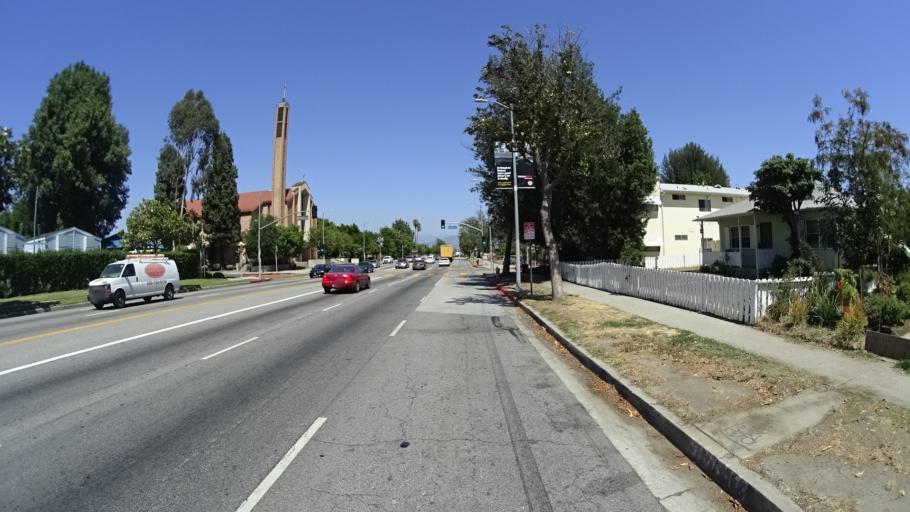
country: US
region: California
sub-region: Los Angeles County
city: Van Nuys
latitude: 34.2215
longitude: -118.4411
